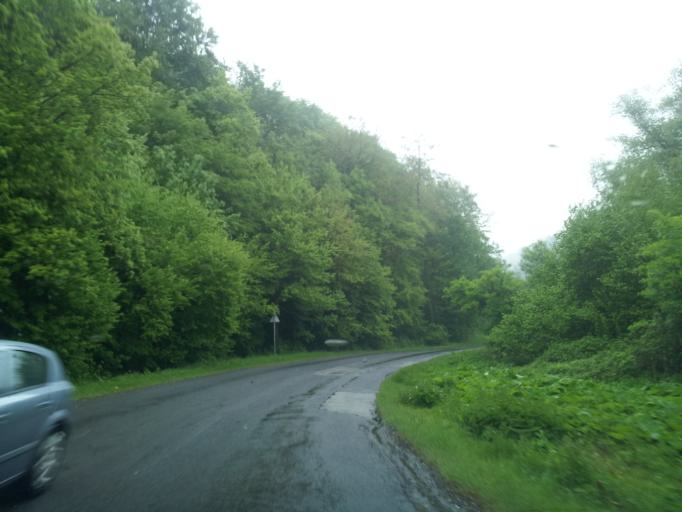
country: HU
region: Baranya
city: Komlo
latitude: 46.2151
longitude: 18.3000
